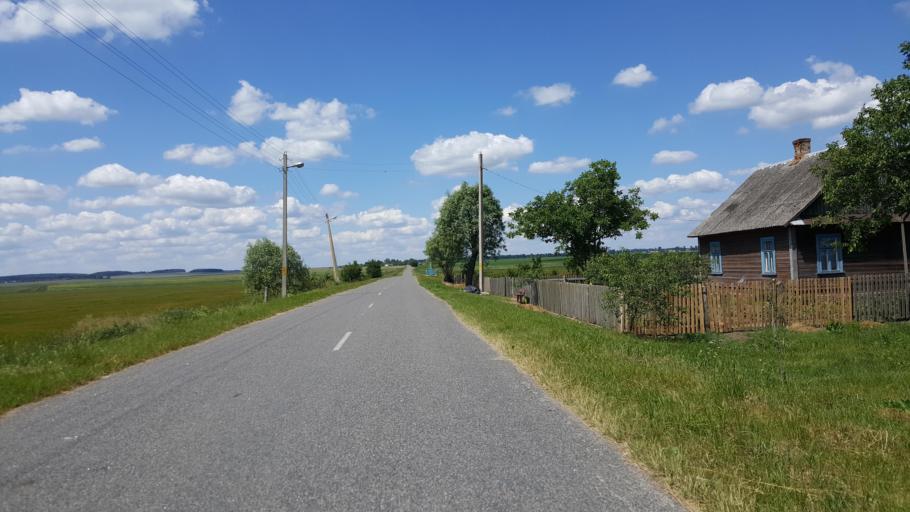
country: BY
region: Brest
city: Vysokaye
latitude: 52.4450
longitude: 23.5392
